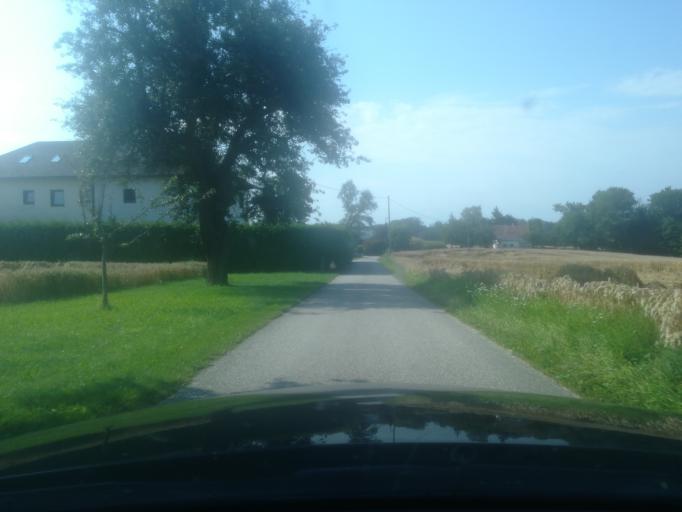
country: AT
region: Upper Austria
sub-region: Wels-Land
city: Holzhausen
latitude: 48.2306
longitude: 14.0778
